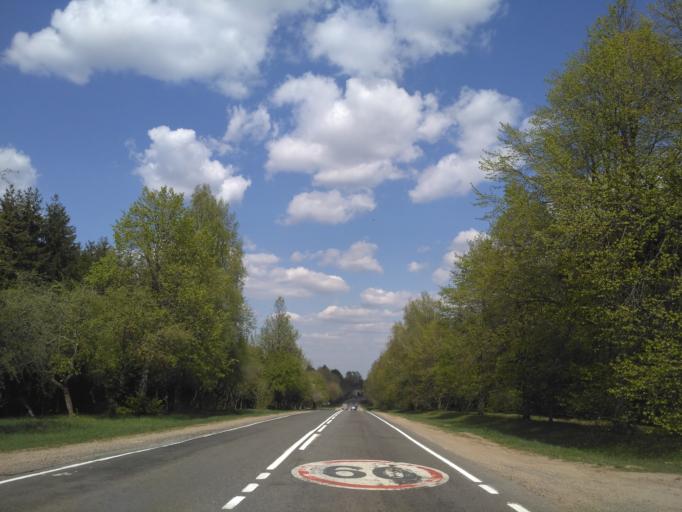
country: BY
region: Minsk
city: Vilyeyka
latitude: 54.5882
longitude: 26.8743
